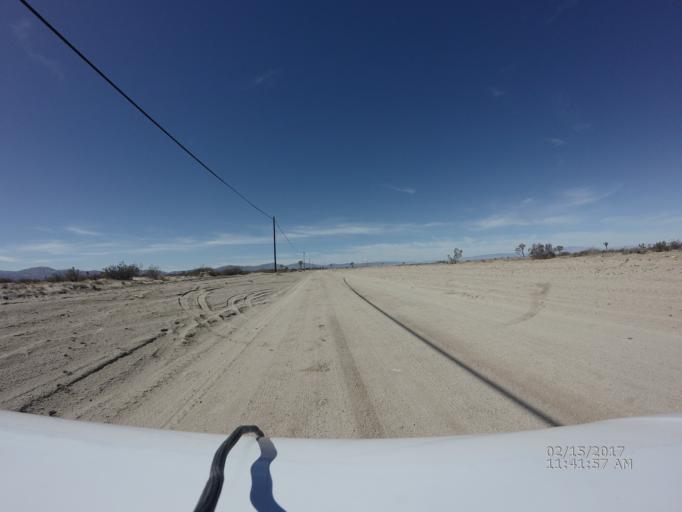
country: US
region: California
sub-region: Los Angeles County
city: Littlerock
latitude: 34.5872
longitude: -117.9425
